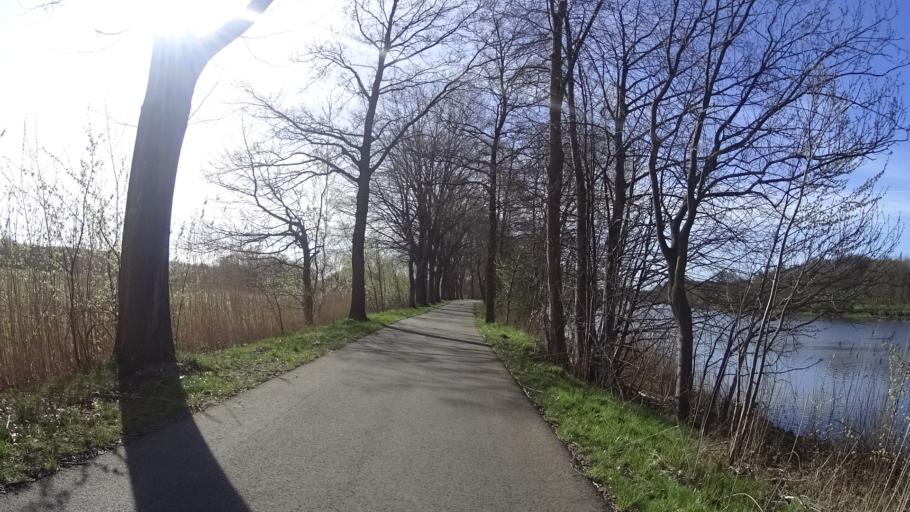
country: DE
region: Lower Saxony
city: Meppen
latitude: 52.7276
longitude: 7.2648
